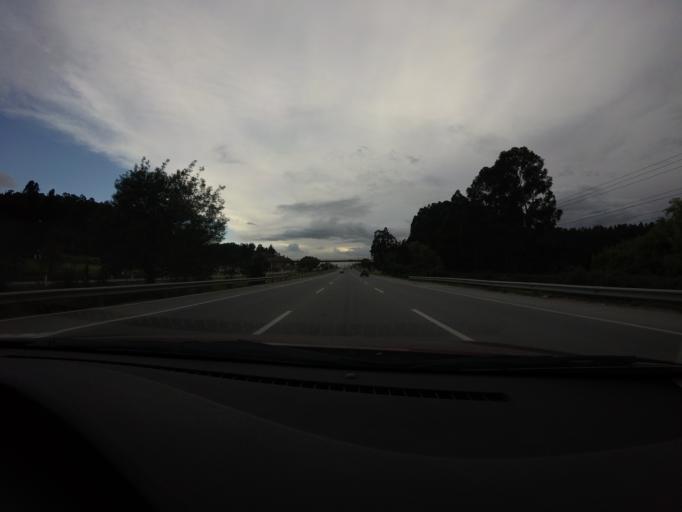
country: CO
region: Cundinamarca
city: Cajica
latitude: 4.9371
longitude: -73.9828
